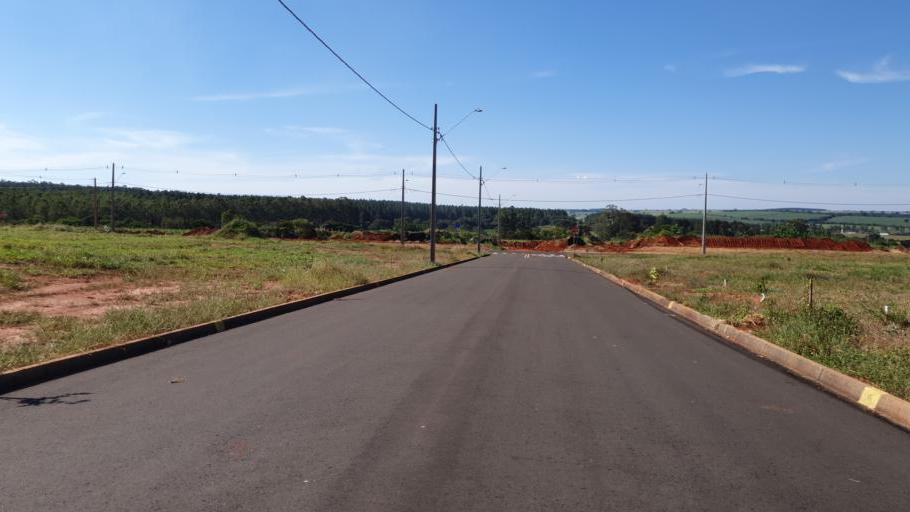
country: BR
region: Sao Paulo
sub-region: Paraguacu Paulista
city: Paraguacu Paulista
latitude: -22.4003
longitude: -50.5761
